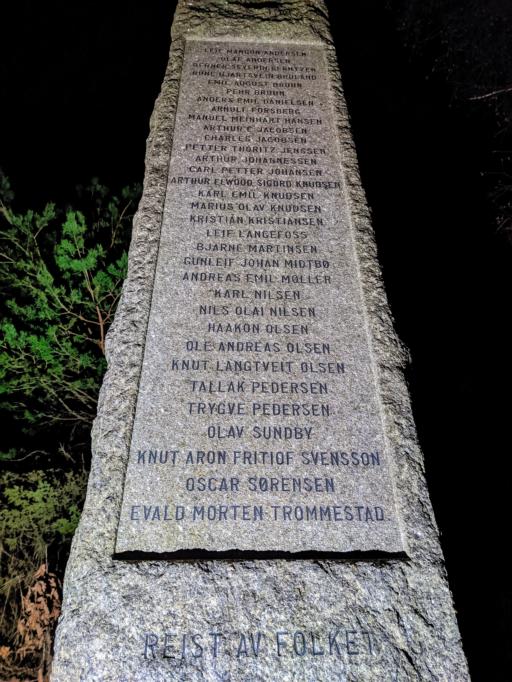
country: NO
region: Aust-Agder
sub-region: Arendal
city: Arendal
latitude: 58.4344
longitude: 8.7486
